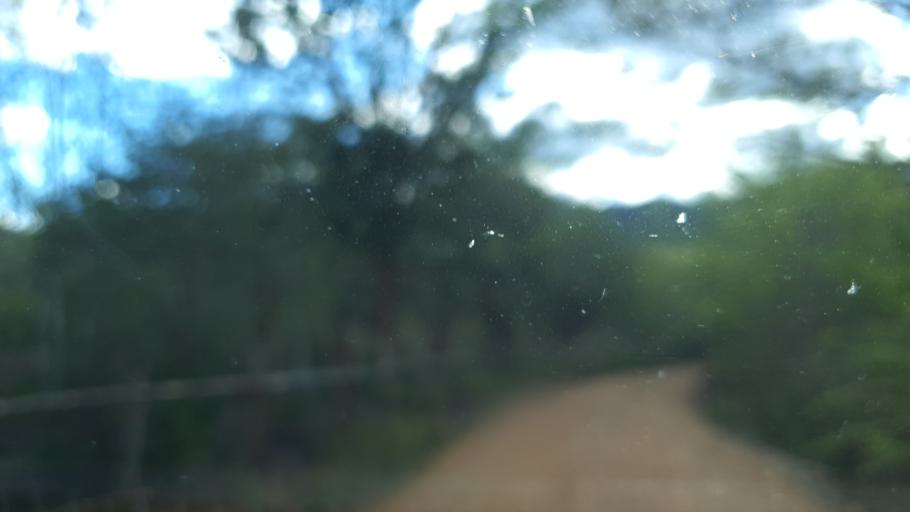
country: TH
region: Lampang
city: Sop Prap
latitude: 17.8559
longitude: 99.2882
